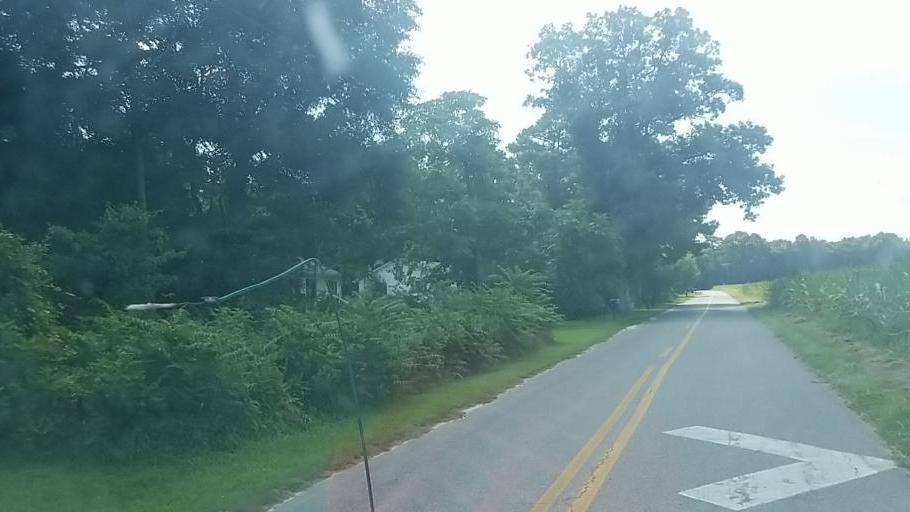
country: US
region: Maryland
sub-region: Worcester County
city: Snow Hill
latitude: 38.2526
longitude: -75.3867
